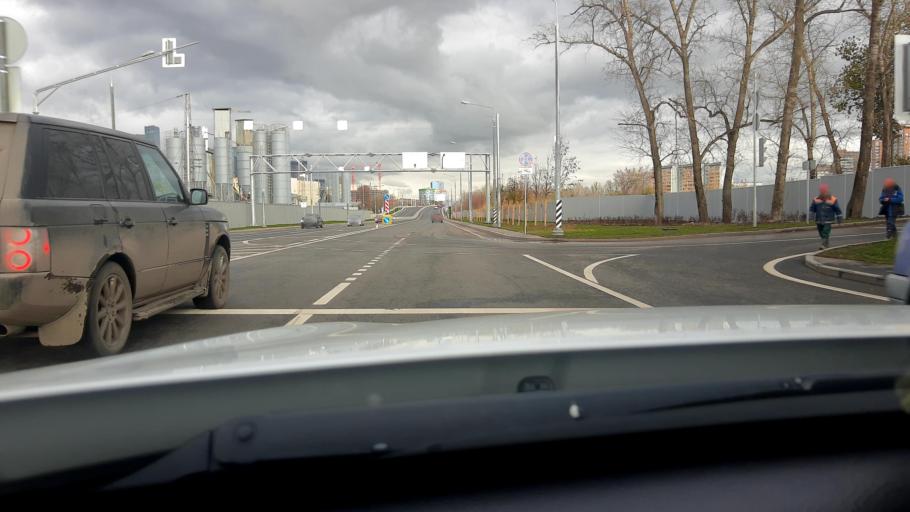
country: RU
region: Moskovskaya
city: Kastanayevo
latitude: 55.7263
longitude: 37.5110
